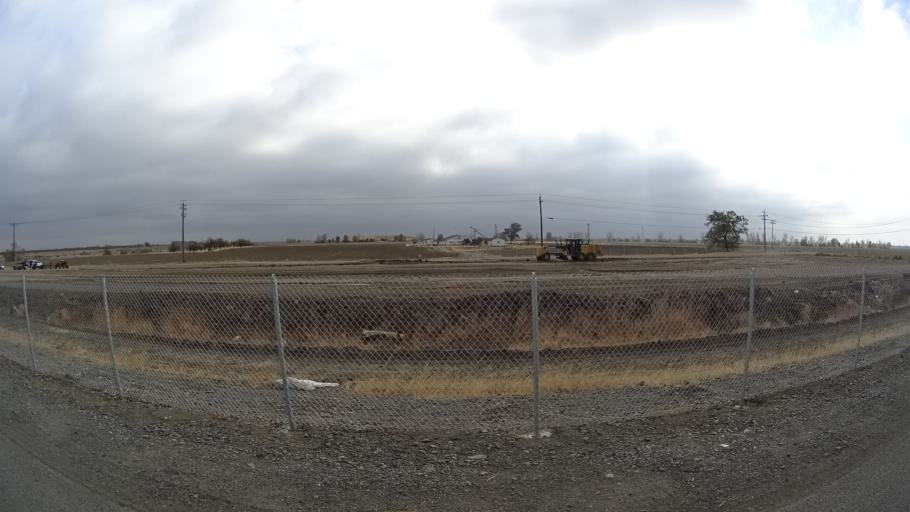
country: US
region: California
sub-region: Yolo County
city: Esparto
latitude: 38.7104
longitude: -122.0124
